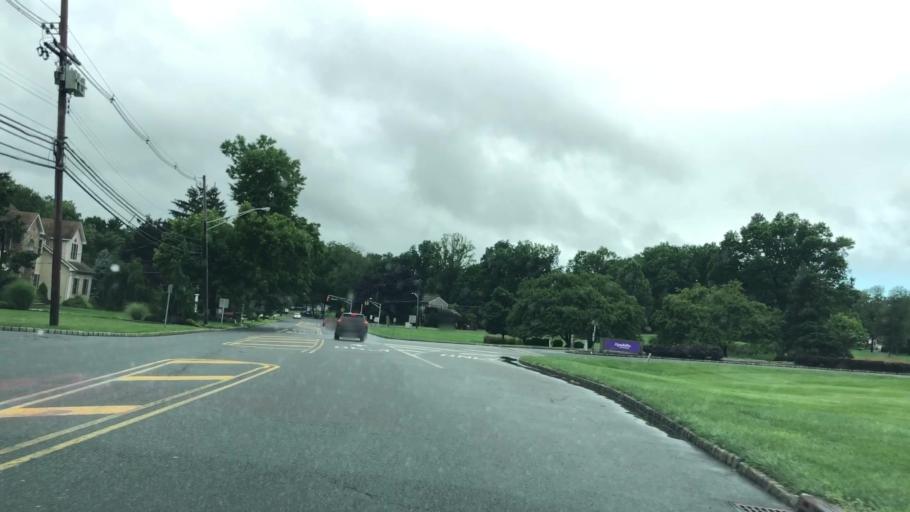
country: US
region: New Jersey
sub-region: Morris County
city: East Hanover
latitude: 40.8127
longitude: -74.3593
